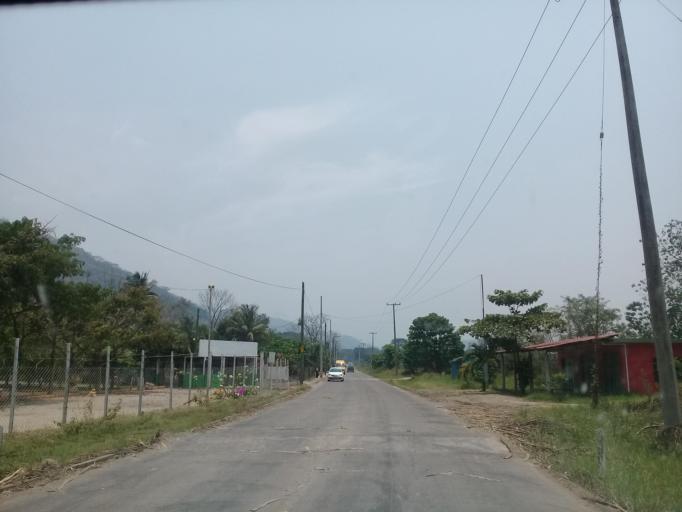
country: MX
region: Veracruz
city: Cosolapa
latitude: 18.5876
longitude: -96.6985
